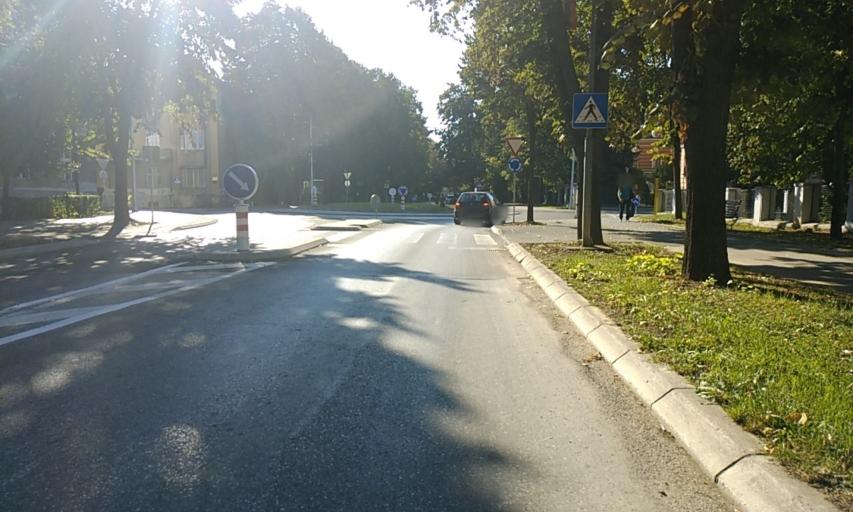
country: BA
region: Republika Srpska
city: Banja Luka
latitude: 44.7741
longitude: 17.1972
